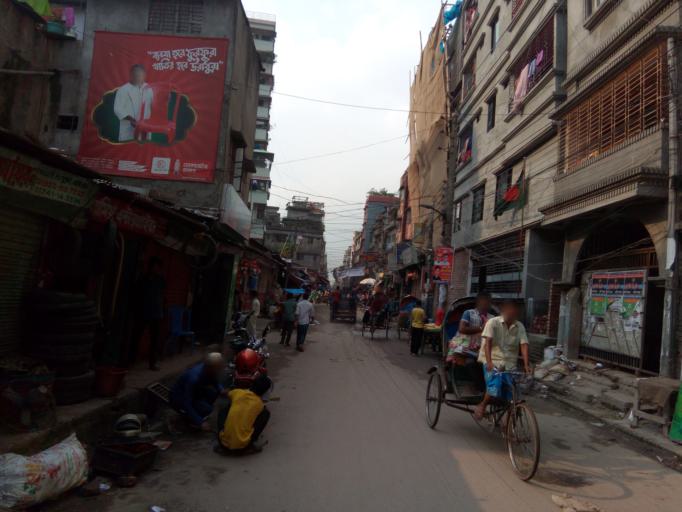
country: BD
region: Dhaka
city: Paltan
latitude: 23.7284
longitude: 90.4341
